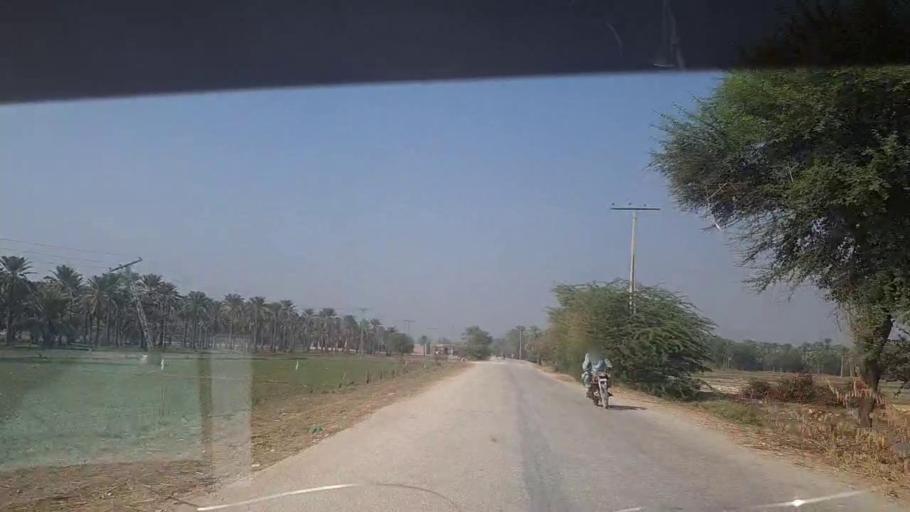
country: PK
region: Sindh
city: Kot Diji
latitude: 27.3609
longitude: 68.7079
